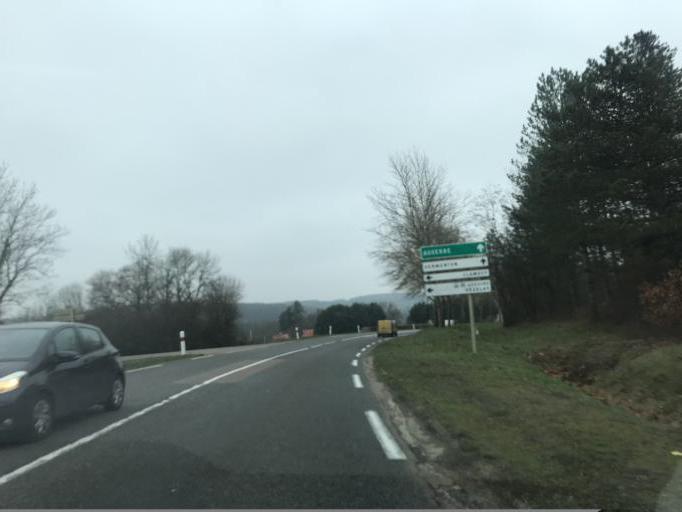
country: FR
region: Bourgogne
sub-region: Departement de l'Yonne
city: Avallon
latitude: 47.5241
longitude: 3.7954
